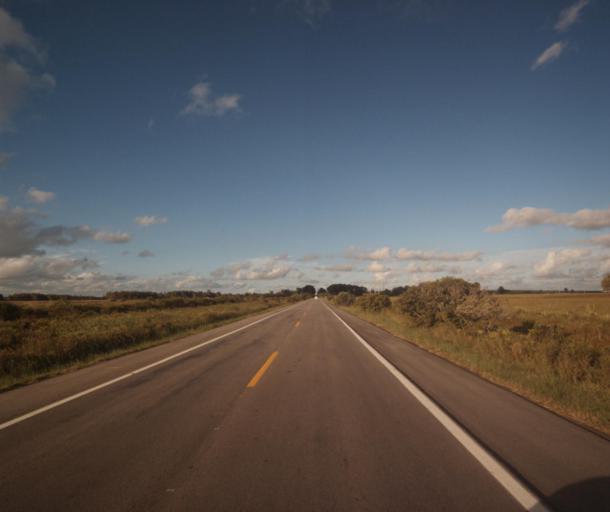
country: BR
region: Rio Grande do Sul
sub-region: Rio Grande
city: Rio Grande
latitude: -32.1300
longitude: -52.3694
